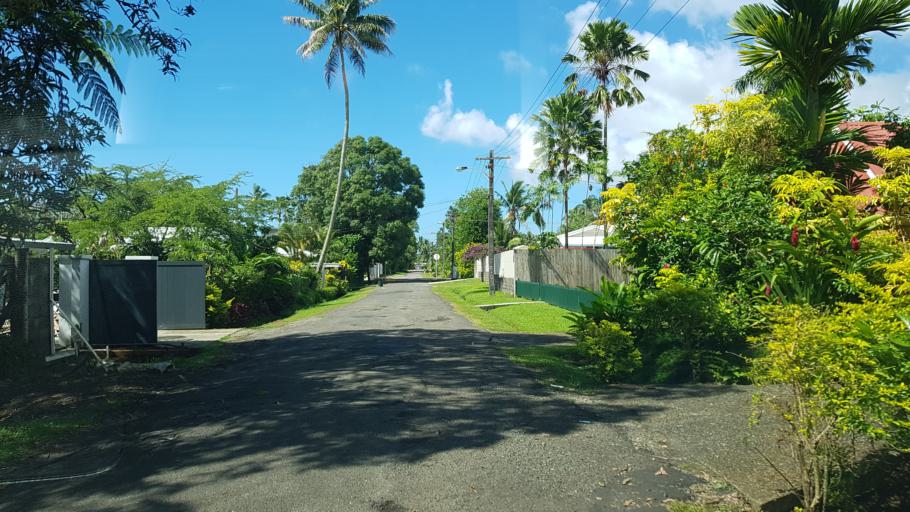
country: FJ
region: Central
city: Suva
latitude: -18.1459
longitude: 178.4556
